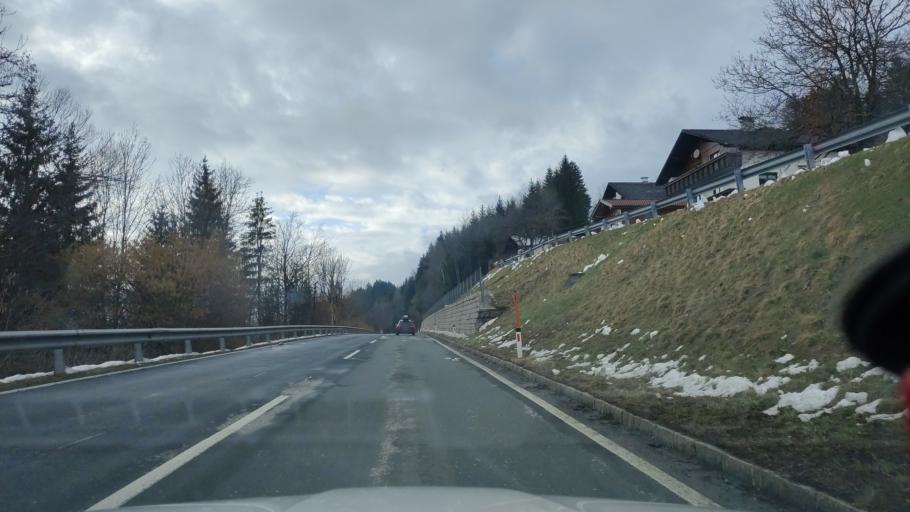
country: AT
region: Carinthia
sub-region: Politischer Bezirk Hermagor
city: Hermagor
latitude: 46.6218
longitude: 13.3051
